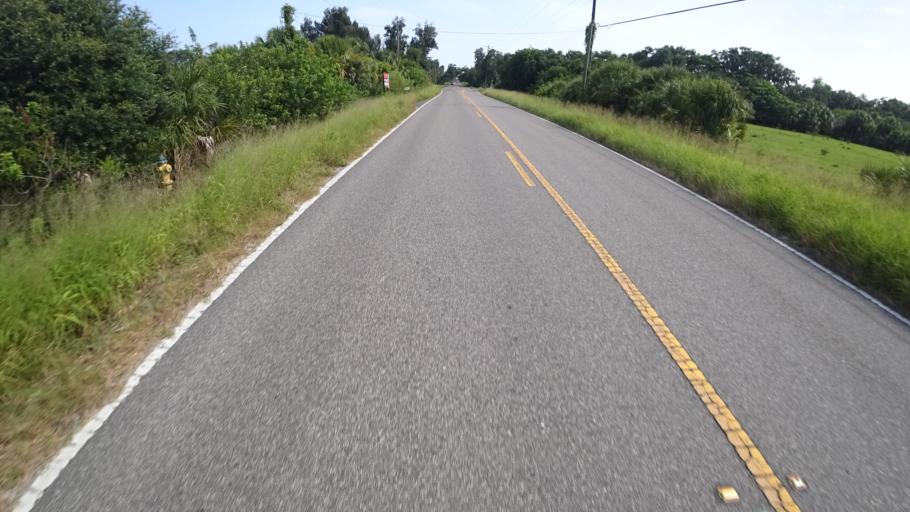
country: US
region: Florida
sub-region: Manatee County
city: Ellenton
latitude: 27.5388
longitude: -82.5283
